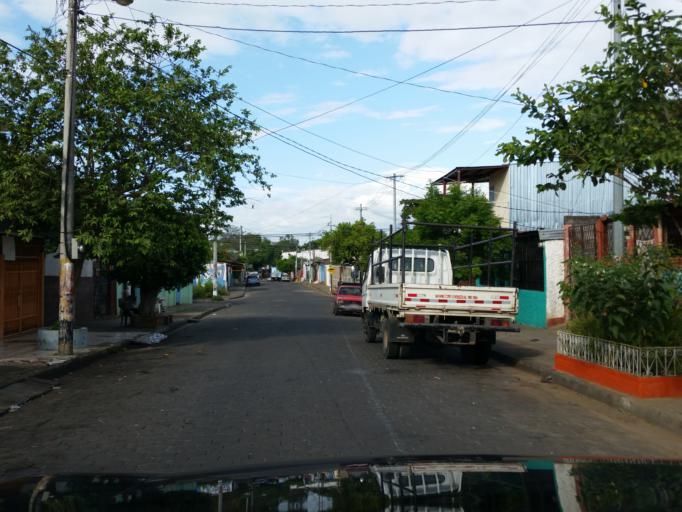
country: NI
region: Managua
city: Managua
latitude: 12.1297
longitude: -86.2584
